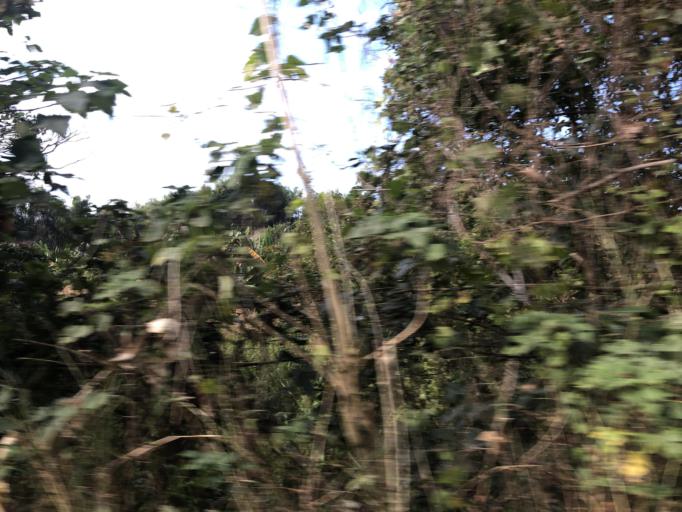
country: TW
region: Taiwan
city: Yujing
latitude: 23.0371
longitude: 120.4185
